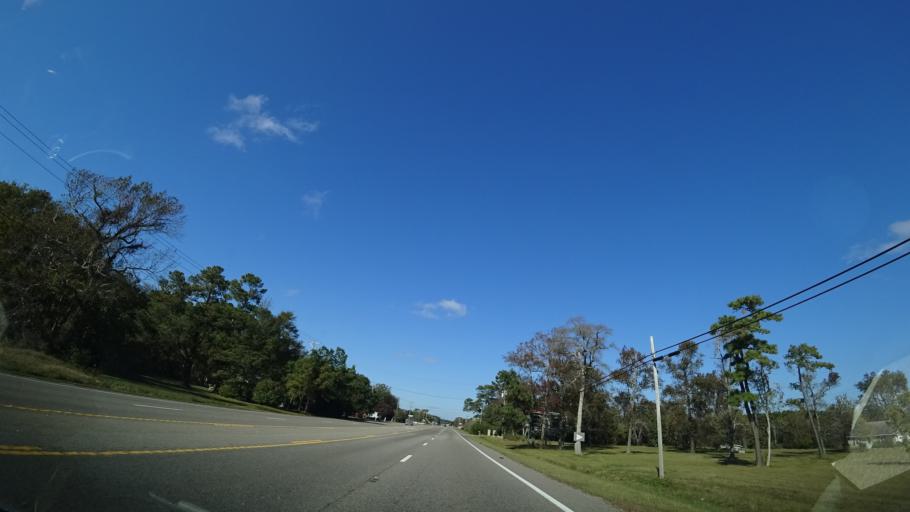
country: US
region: North Carolina
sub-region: Dare County
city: Southern Shores
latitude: 36.1658
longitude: -75.8588
